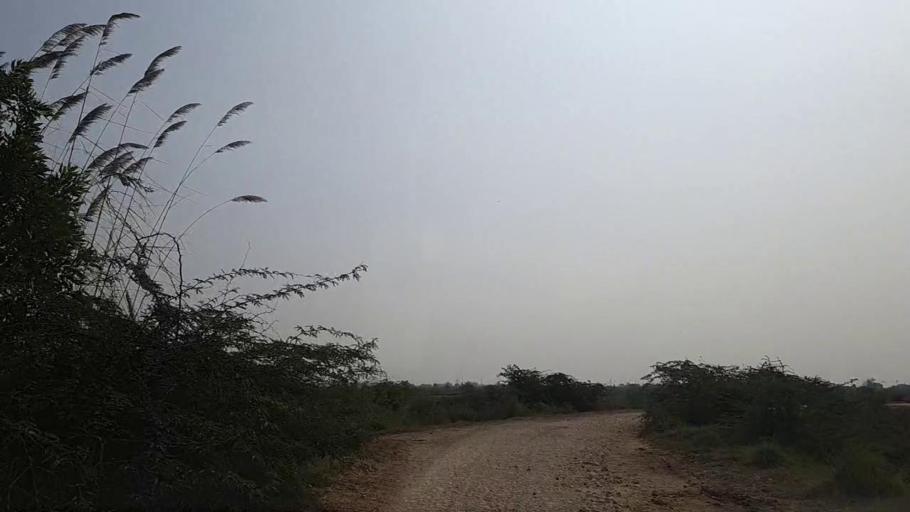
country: PK
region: Sindh
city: Mirpur Sakro
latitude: 24.5913
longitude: 67.7191
